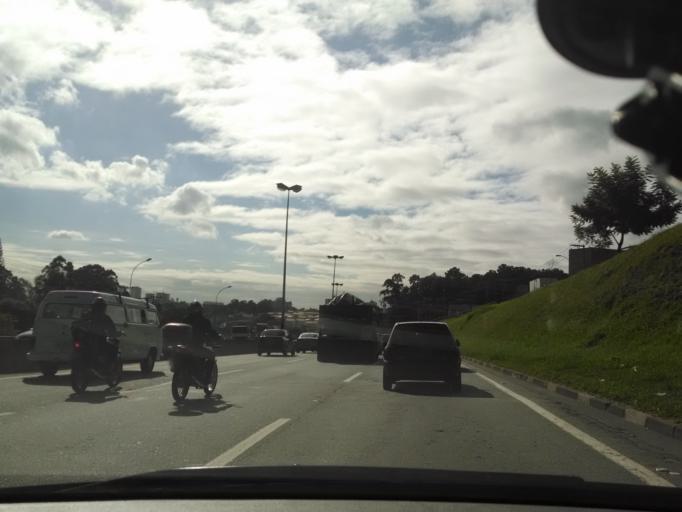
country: BR
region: Sao Paulo
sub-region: Taboao Da Serra
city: Taboao da Serra
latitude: -23.5931
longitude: -46.8053
